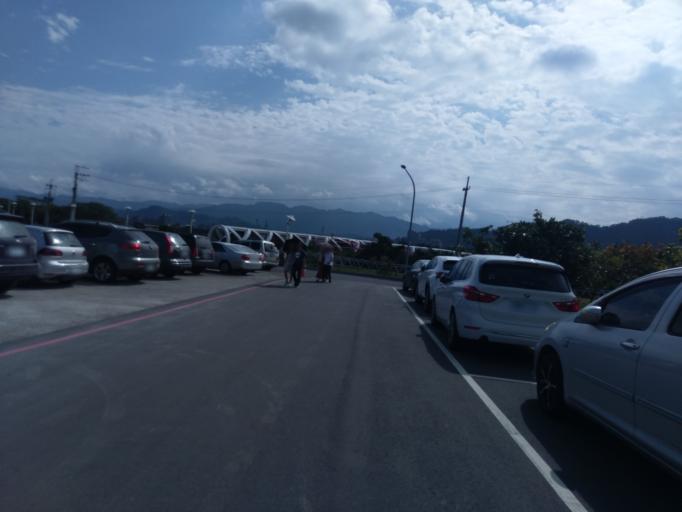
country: TW
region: Taiwan
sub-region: Taoyuan
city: Taoyuan
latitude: 24.9514
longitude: 121.3564
